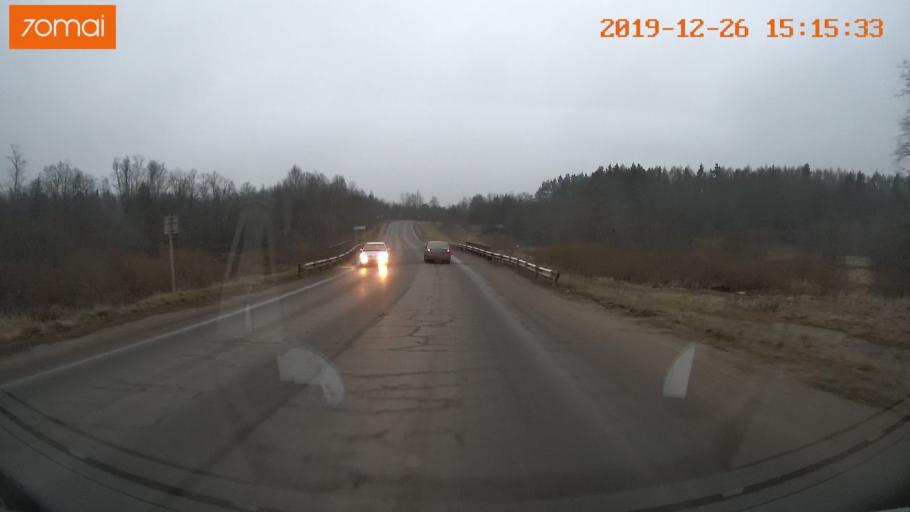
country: RU
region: Jaroslavl
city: Rybinsk
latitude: 58.0956
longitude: 38.8743
